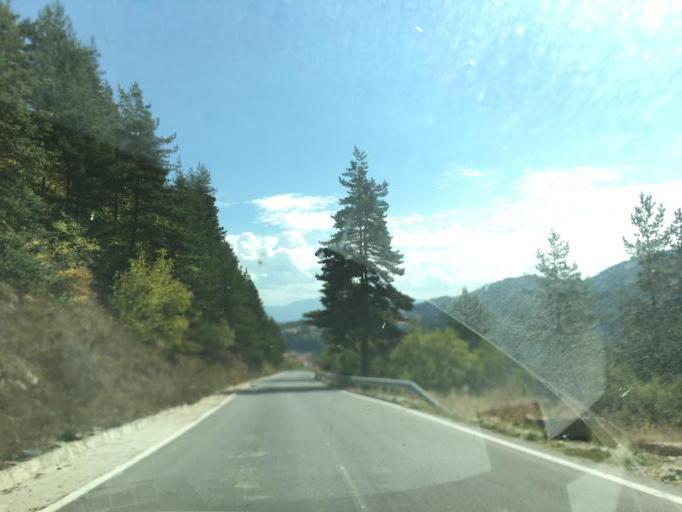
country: BG
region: Pazardzhik
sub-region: Obshtina Bratsigovo
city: Bratsigovo
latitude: 41.8857
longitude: 24.3428
